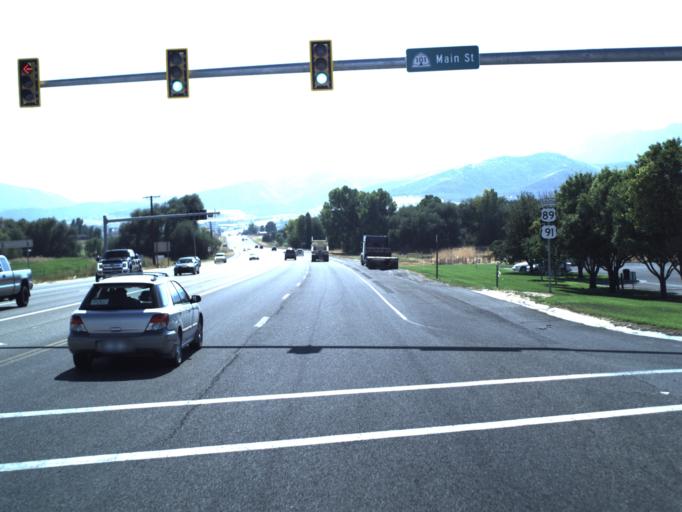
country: US
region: Utah
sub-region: Cache County
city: Wellsville
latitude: 41.6449
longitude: -111.9142
